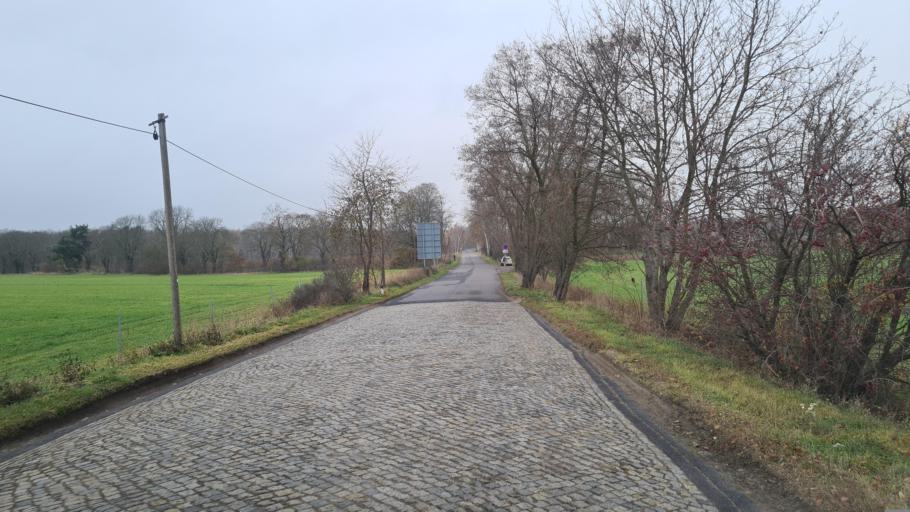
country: DE
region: Brandenburg
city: Lubbenau
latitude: 51.8323
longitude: 13.9106
